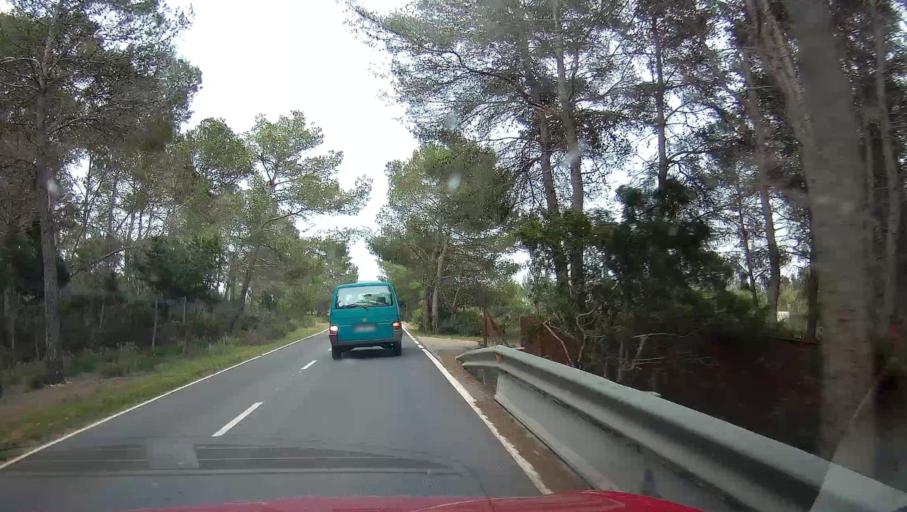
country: ES
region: Balearic Islands
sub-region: Illes Balears
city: Sant Joan de Labritja
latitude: 39.0464
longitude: 1.4102
